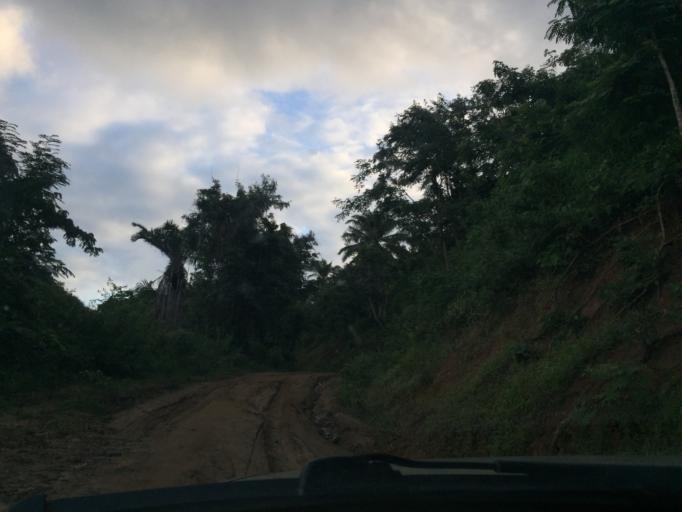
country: TZ
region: Tanga
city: Muheza
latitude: -5.1311
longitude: 38.7706
